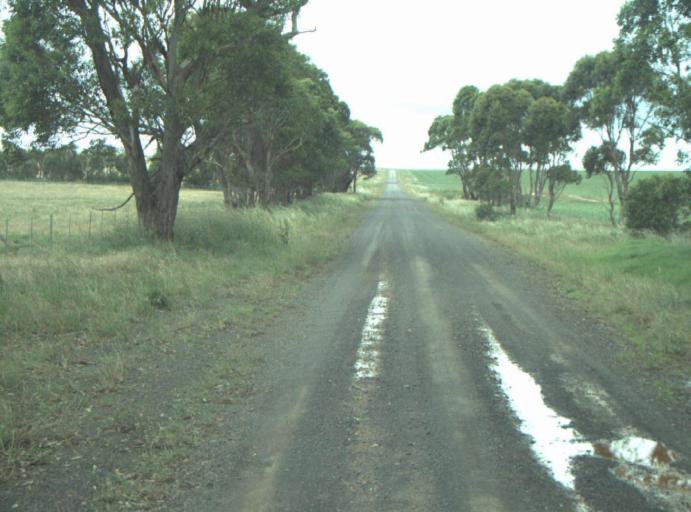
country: AU
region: Victoria
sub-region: Greater Geelong
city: Lara
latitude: -37.8826
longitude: 144.3502
